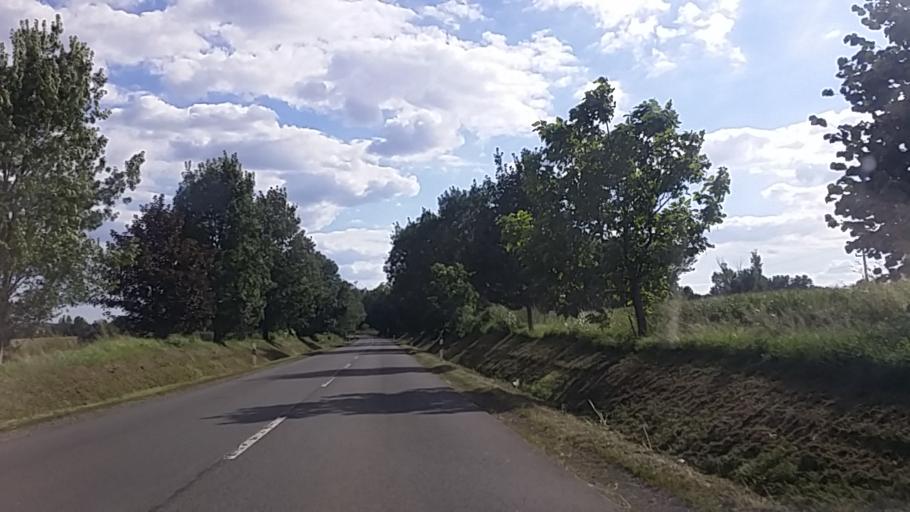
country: HU
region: Baranya
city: Sasd
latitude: 46.2749
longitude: 18.1055
